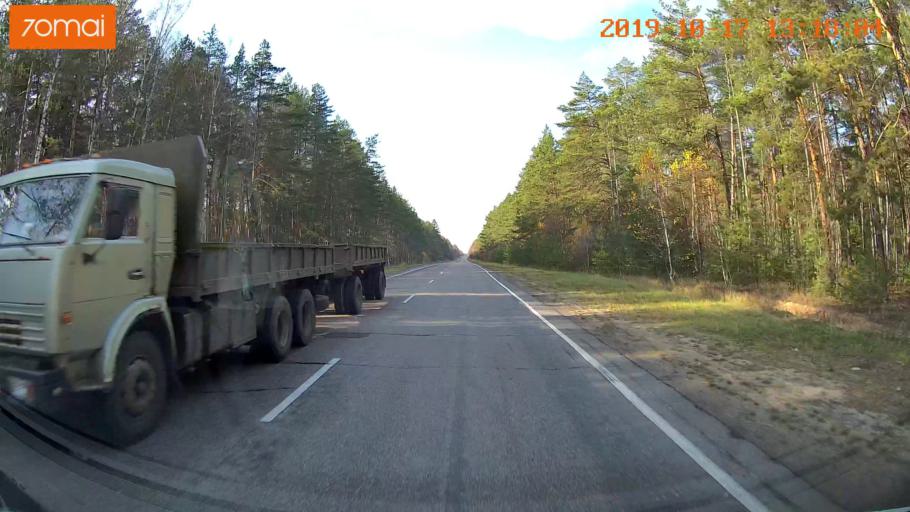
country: RU
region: Rjazan
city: Gus'-Zheleznyy
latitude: 55.0606
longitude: 41.1065
